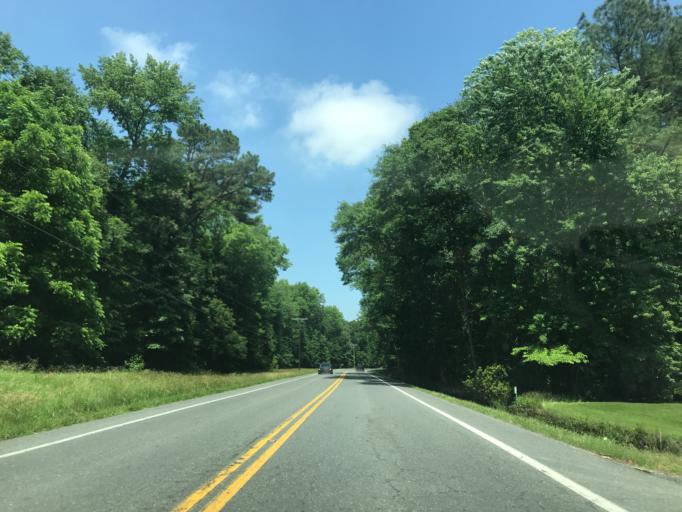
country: US
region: Maryland
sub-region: Dorchester County
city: Hurlock
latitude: 38.6304
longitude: -75.8129
